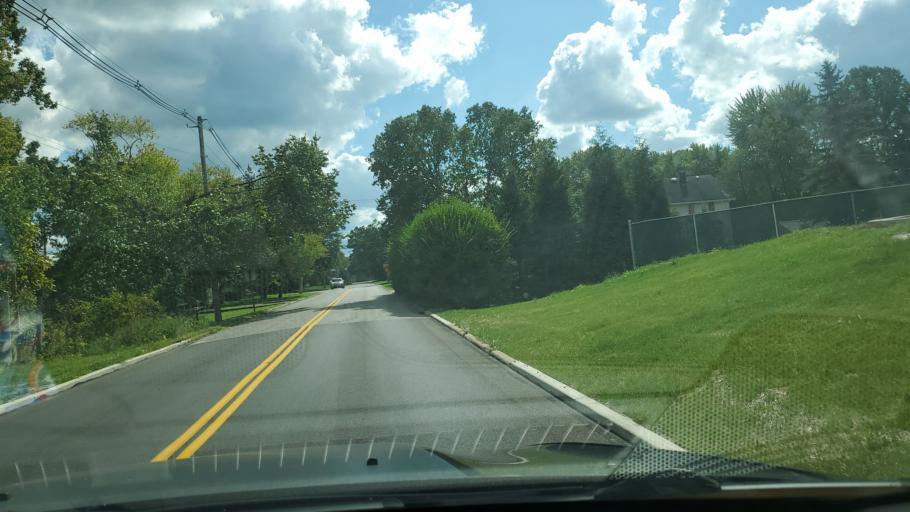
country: US
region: Ohio
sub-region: Mahoning County
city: Boardman
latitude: 41.0175
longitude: -80.6565
